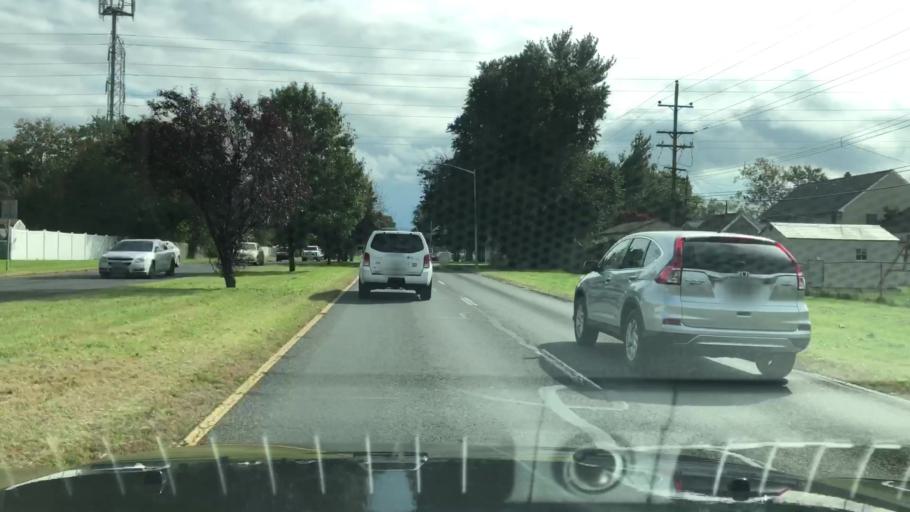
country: US
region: Pennsylvania
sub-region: Bucks County
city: Levittown
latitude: 40.1595
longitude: -74.8317
